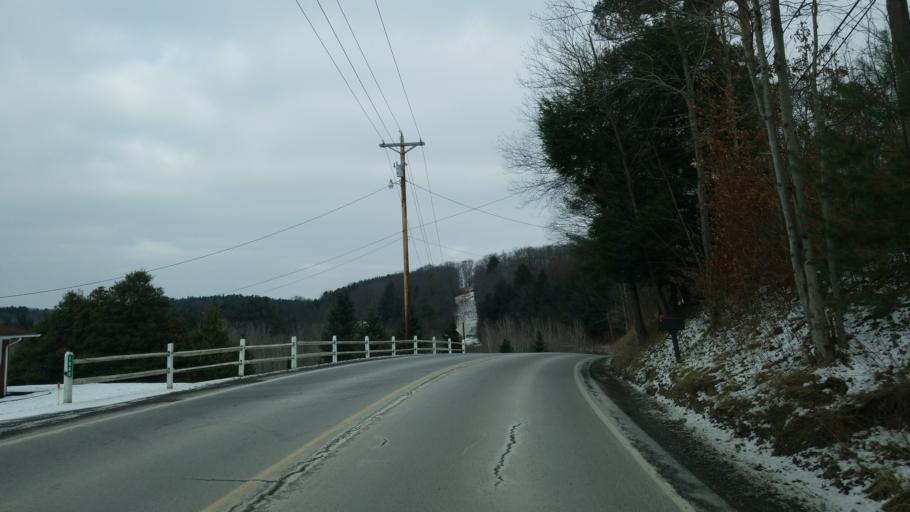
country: US
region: Pennsylvania
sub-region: Clearfield County
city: DuBois
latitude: 41.0924
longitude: -78.7349
